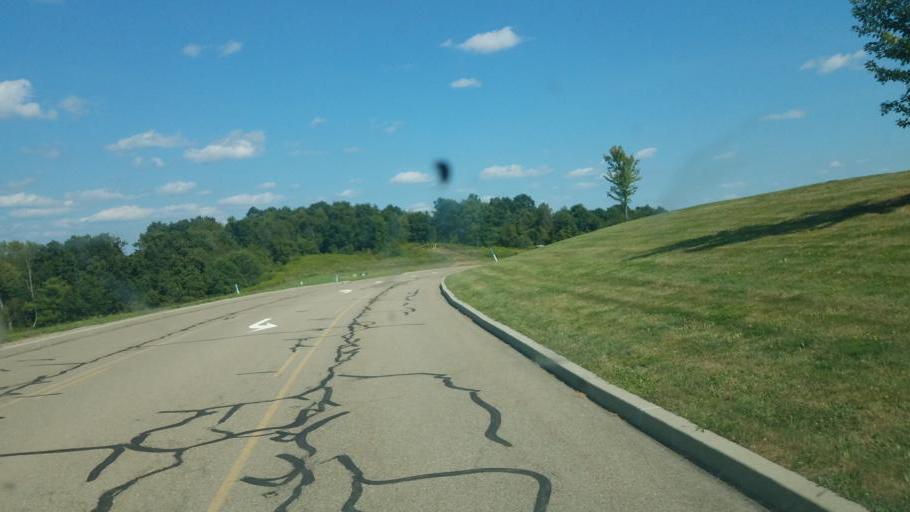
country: US
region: Pennsylvania
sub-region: Clarion County
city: Clarion
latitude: 41.1837
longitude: -79.3906
